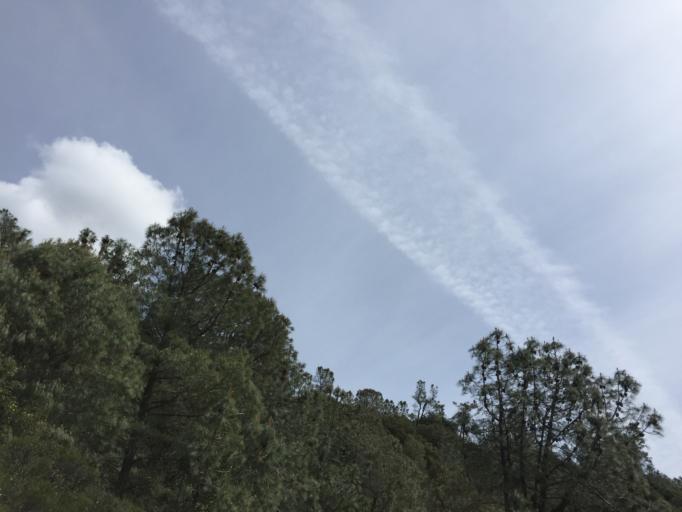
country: US
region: California
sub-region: Contra Costa County
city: Diablo
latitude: 37.8766
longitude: -121.9300
